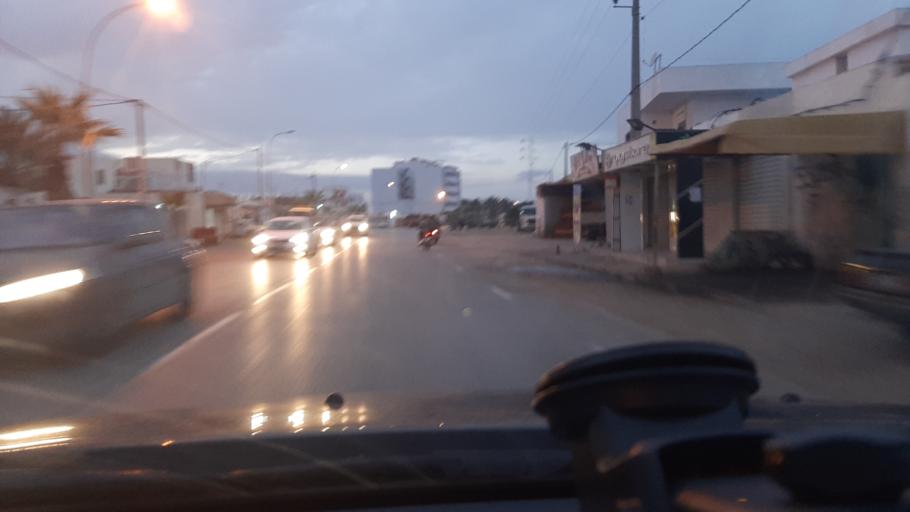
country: TN
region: Safaqis
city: Sfax
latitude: 34.7635
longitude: 10.6902
